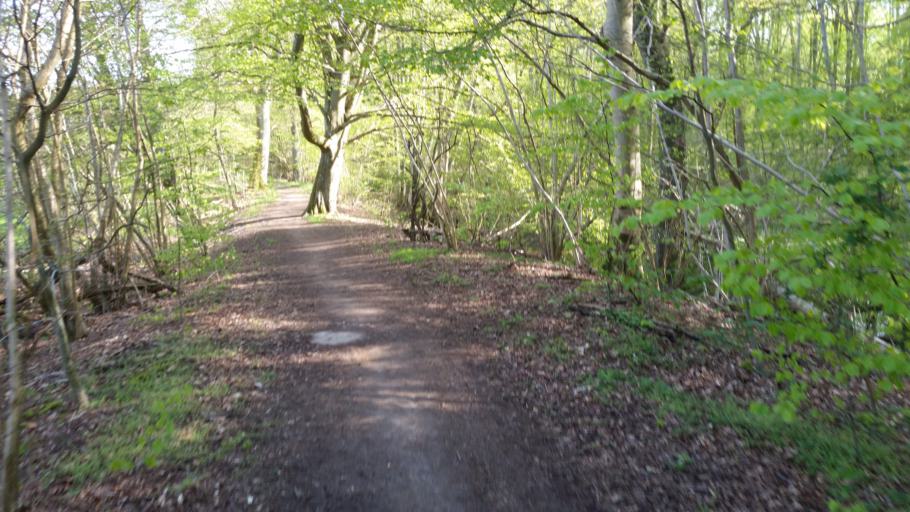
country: DK
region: Capital Region
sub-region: Helsingor Kommune
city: Hornbaek
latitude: 56.0643
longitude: 12.3720
